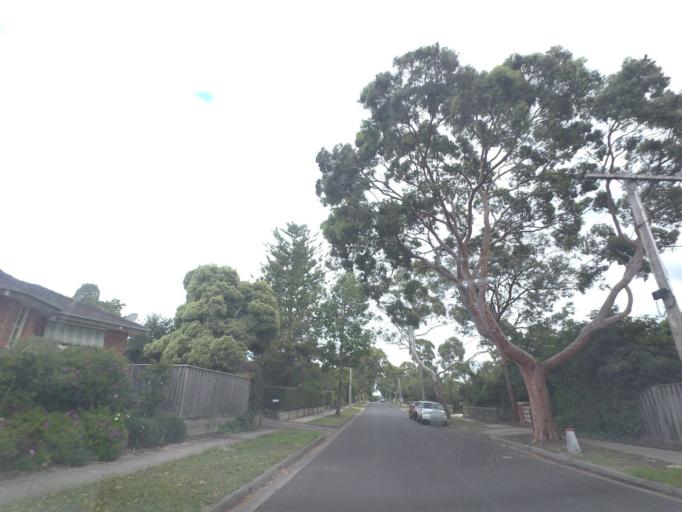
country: AU
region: Victoria
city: Mitcham
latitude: -37.8196
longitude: 145.2062
